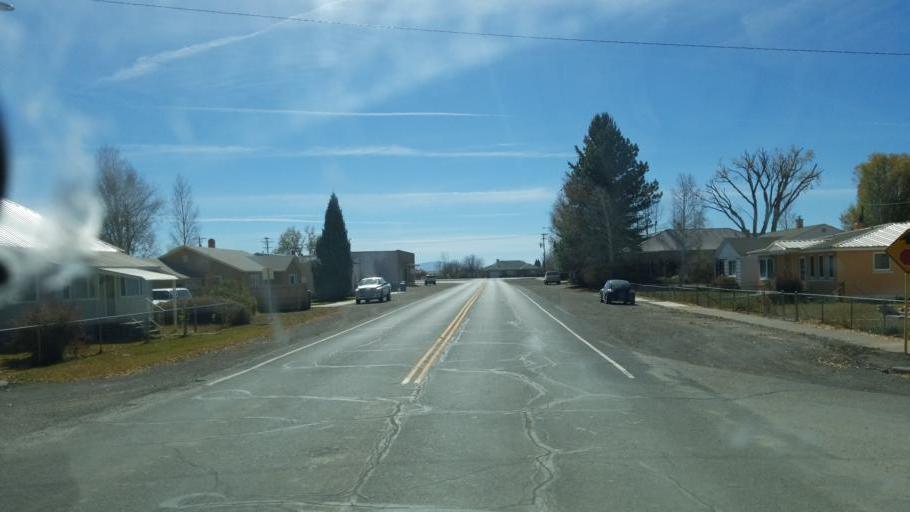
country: US
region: Colorado
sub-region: Conejos County
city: Conejos
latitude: 37.2707
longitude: -105.9603
